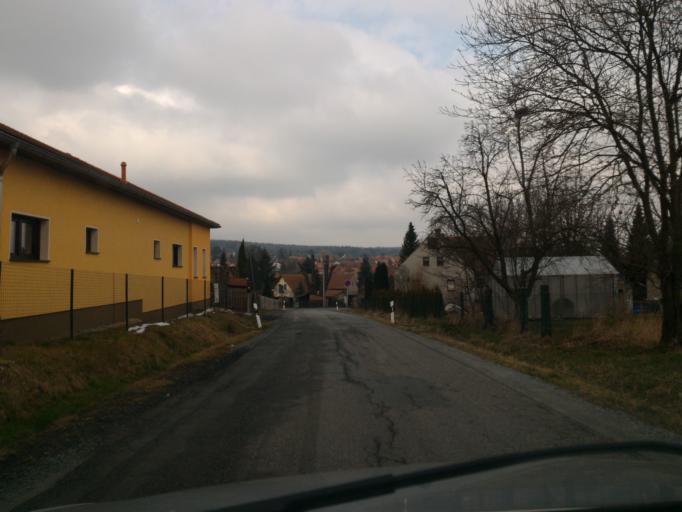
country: DE
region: Saxony
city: Olbersdorf
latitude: 50.8653
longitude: 14.7686
